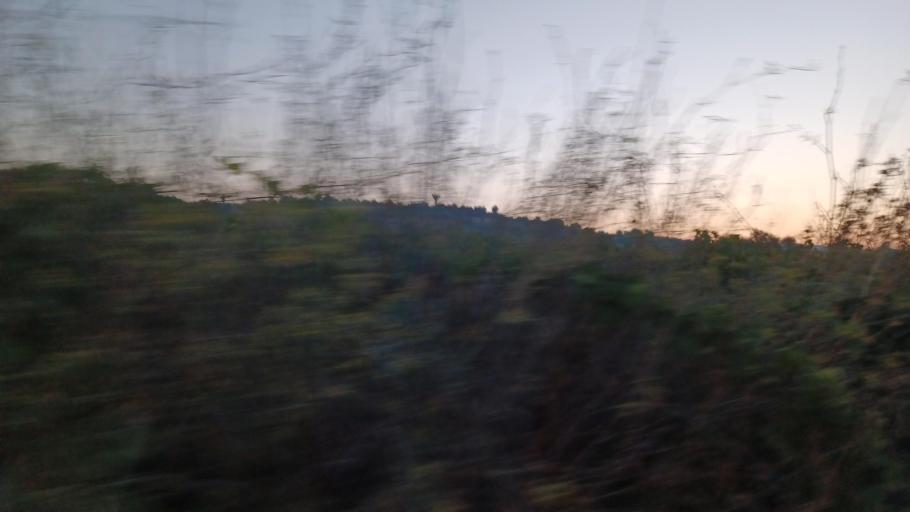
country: CY
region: Pafos
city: Mesogi
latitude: 34.8718
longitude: 32.4972
